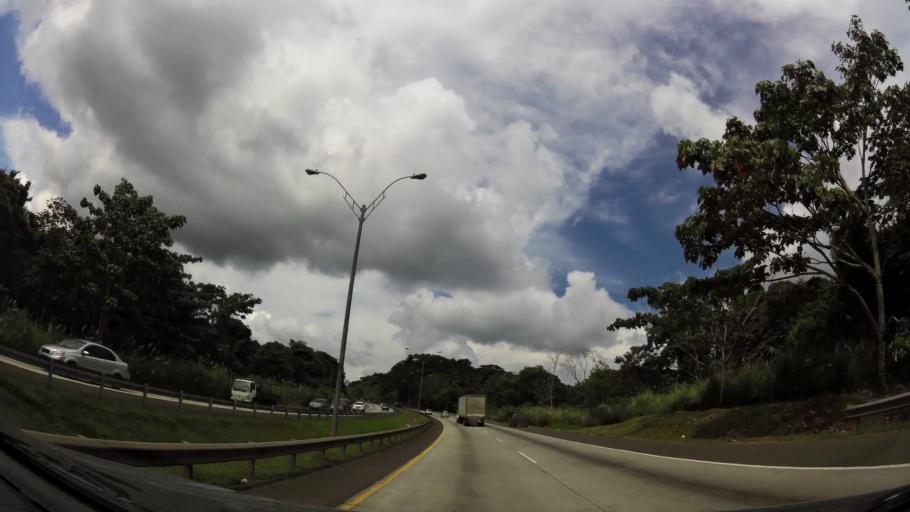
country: PA
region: Panama
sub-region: Distrito Arraijan
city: Arraijan
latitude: 8.9910
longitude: -79.6484
